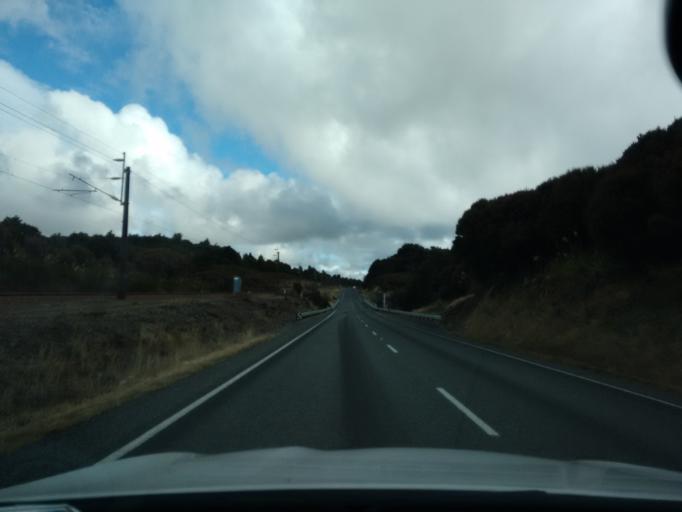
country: NZ
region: Manawatu-Wanganui
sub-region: Ruapehu District
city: Waiouru
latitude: -39.3037
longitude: 175.3898
